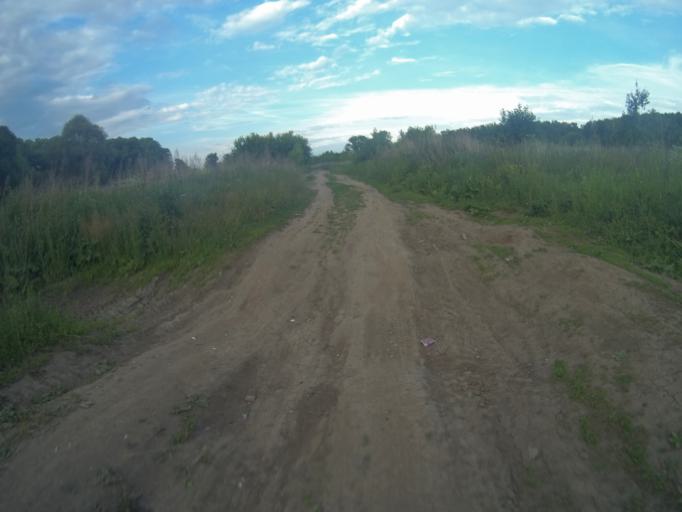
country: RU
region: Vladimir
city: Vladimir
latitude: 56.1939
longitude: 40.3805
